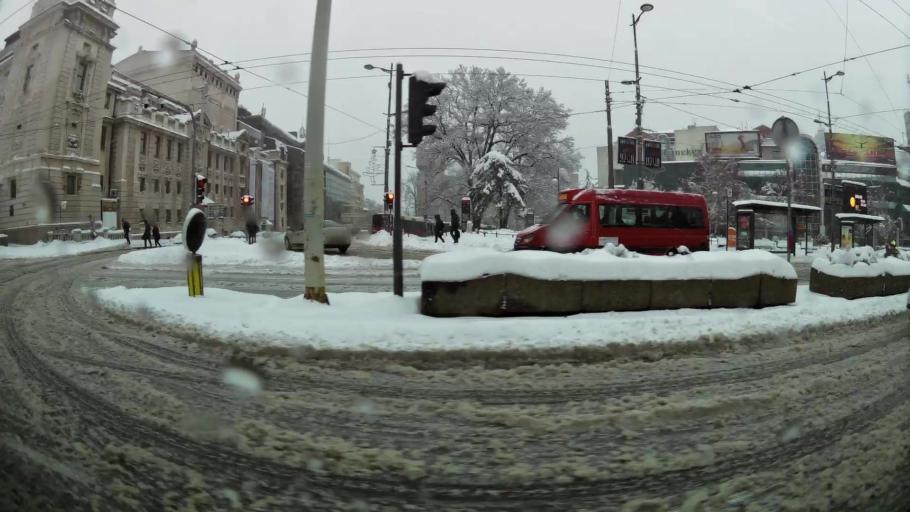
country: RS
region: Central Serbia
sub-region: Belgrade
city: Stari Grad
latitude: 44.8163
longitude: 20.4606
